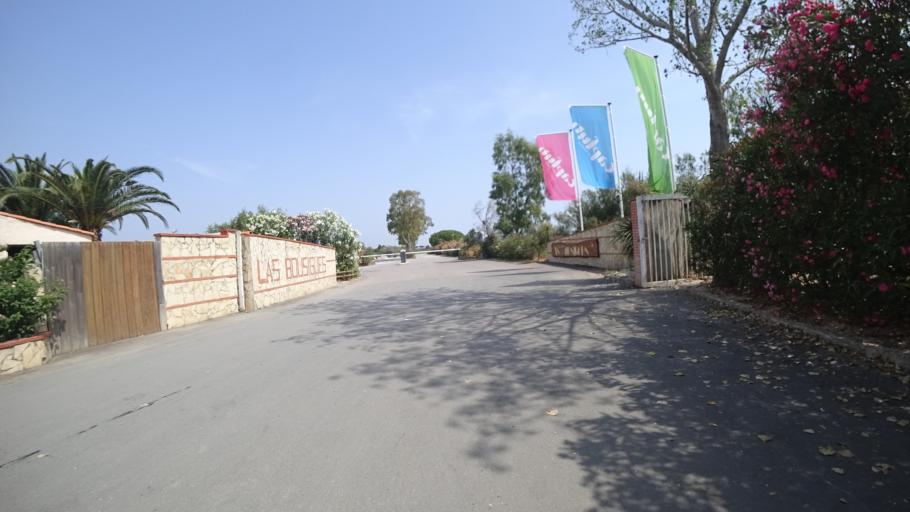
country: FR
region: Languedoc-Roussillon
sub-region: Departement des Pyrenees-Orientales
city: Le Barcares
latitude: 42.7862
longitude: 3.0253
